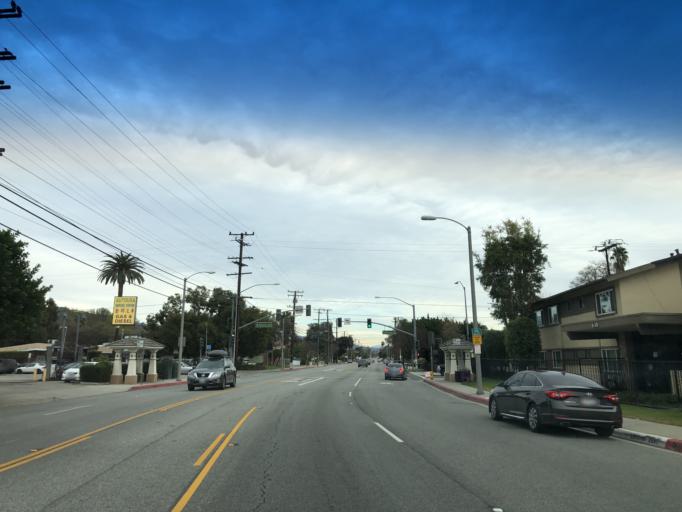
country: US
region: California
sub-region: Los Angeles County
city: Mayflower Village
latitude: 34.1321
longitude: -118.0134
